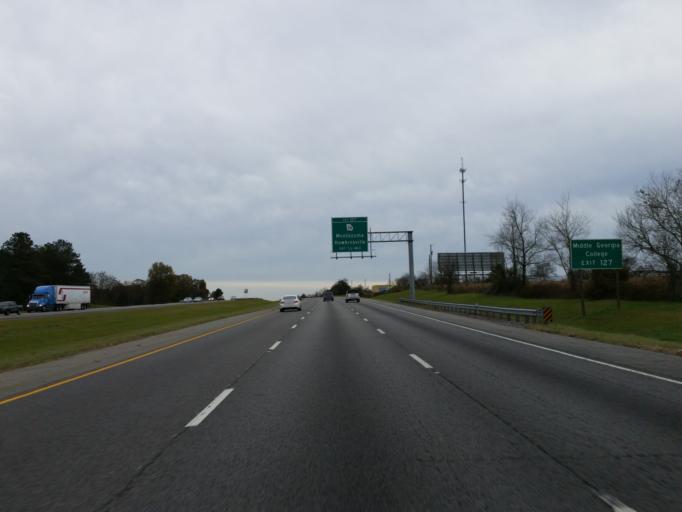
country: US
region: Georgia
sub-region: Dooly County
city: Unadilla
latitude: 32.3468
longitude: -83.7687
